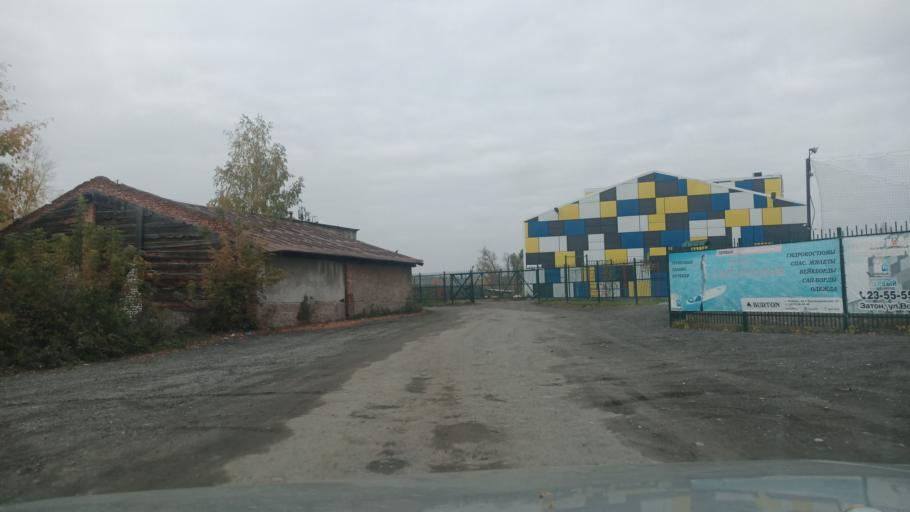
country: RU
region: Altai Krai
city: Zaton
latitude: 53.2991
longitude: 83.8027
